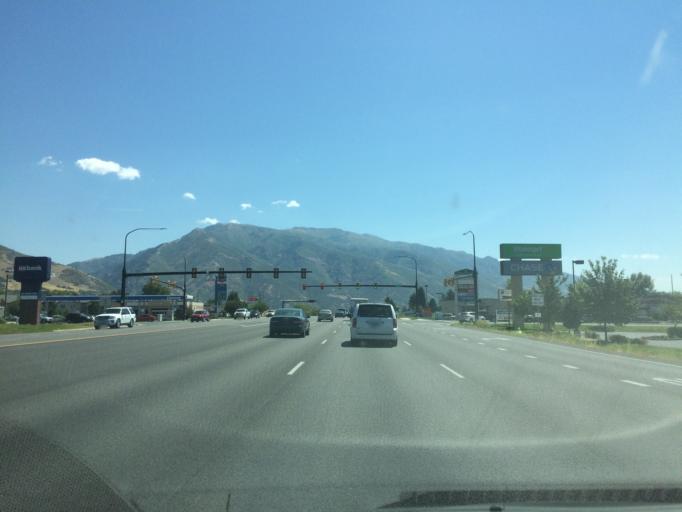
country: US
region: Utah
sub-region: Weber County
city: Uintah
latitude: 41.1526
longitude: -111.9369
